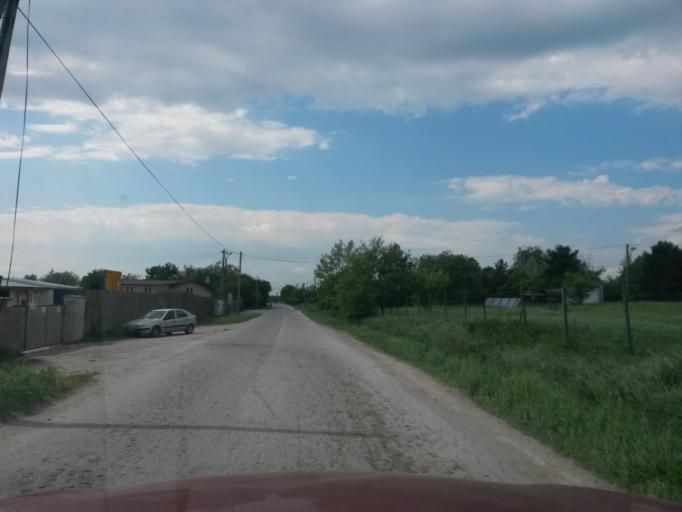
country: SK
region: Kosicky
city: Moldava nad Bodvou
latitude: 48.6978
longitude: 21.0124
